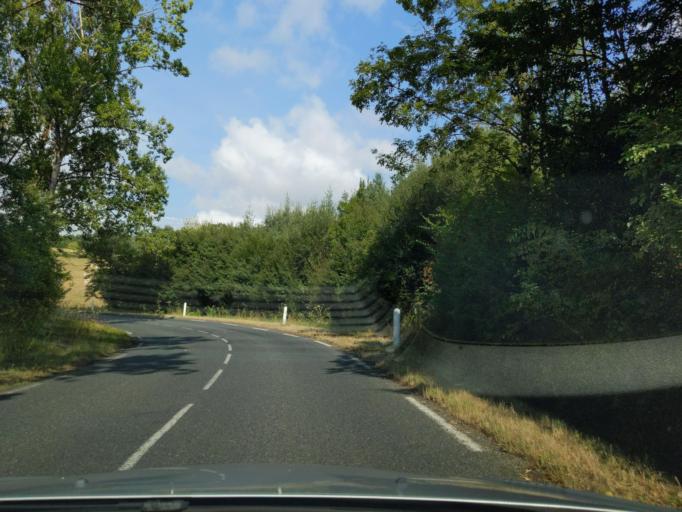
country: FR
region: Bourgogne
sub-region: Departement de la Nievre
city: Luzy
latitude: 46.7071
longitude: 3.8718
